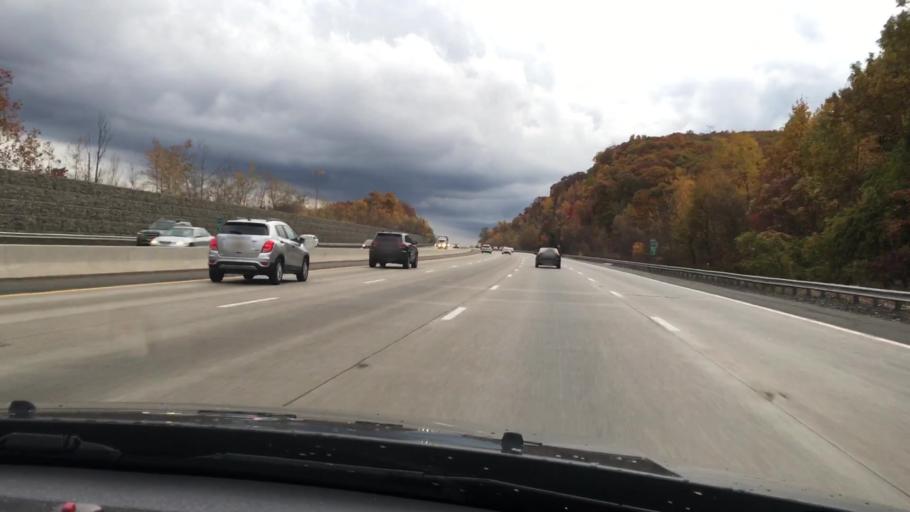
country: US
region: New Jersey
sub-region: Passaic County
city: Bloomingdale
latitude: 40.9619
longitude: -74.3351
